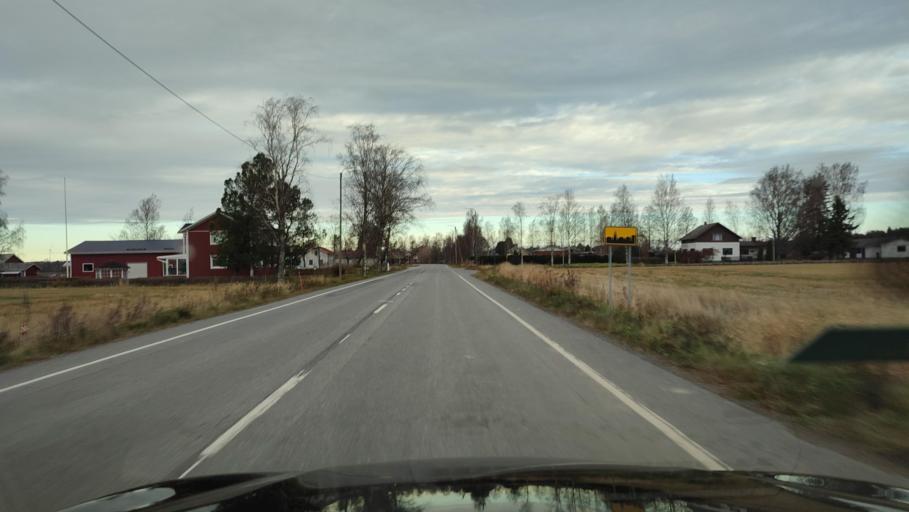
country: FI
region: Ostrobothnia
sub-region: Sydosterbotten
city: Naerpes
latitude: 62.4593
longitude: 21.3555
